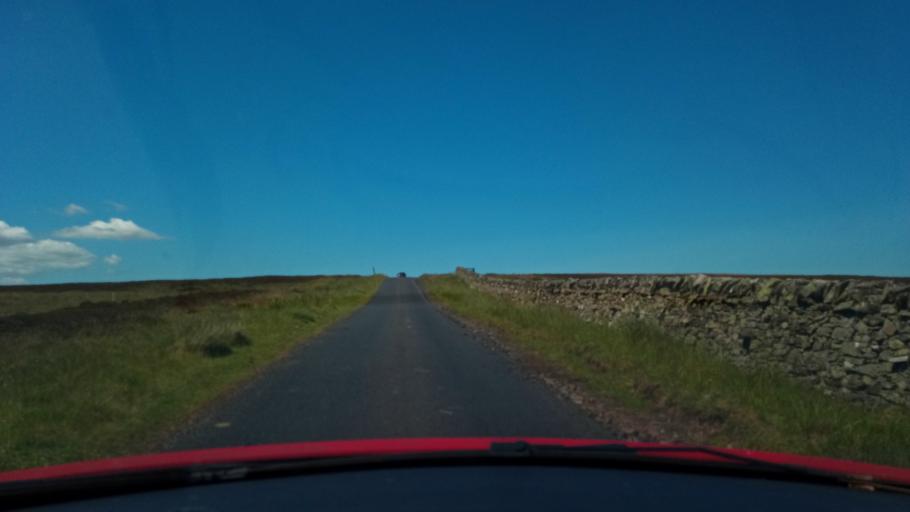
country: GB
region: Scotland
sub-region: East Lothian
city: Dunbar
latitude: 55.8280
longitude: -2.5225
